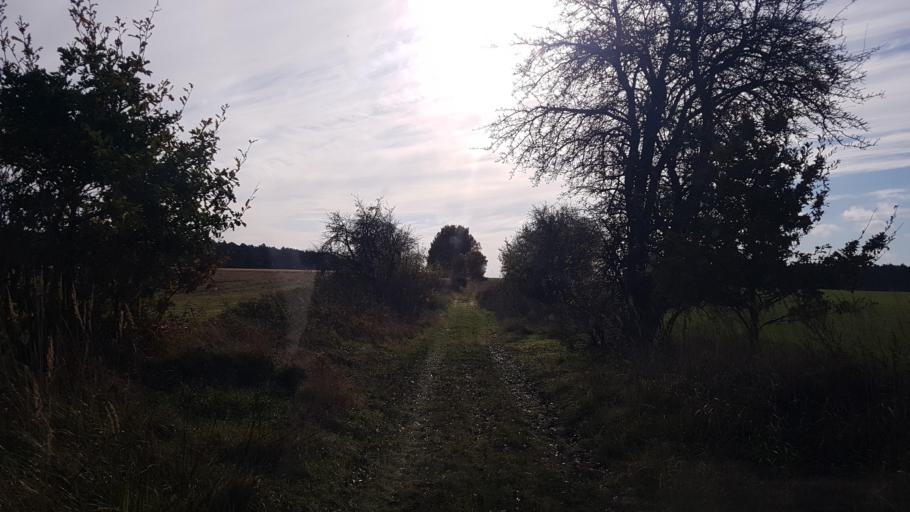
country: DE
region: Saxony-Anhalt
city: Zahna
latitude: 51.9730
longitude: 12.8281
